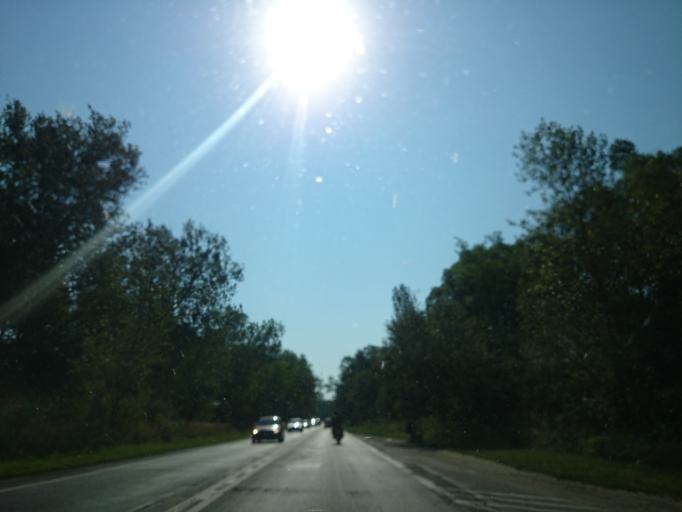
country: PL
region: West Pomeranian Voivodeship
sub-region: Szczecin
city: Szczecin
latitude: 53.3794
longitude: 14.5441
